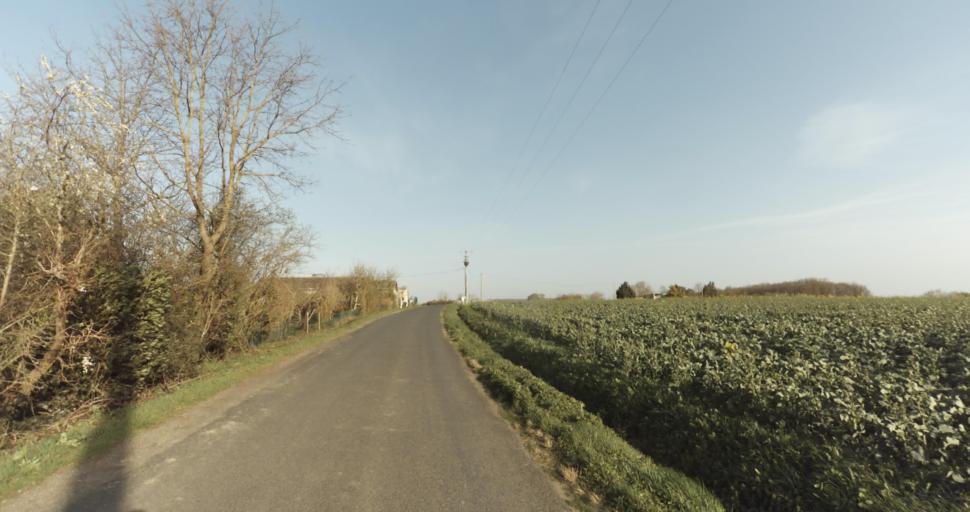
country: FR
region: Midi-Pyrenees
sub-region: Departement du Tarn
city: Saint-Sulpice-la-Pointe
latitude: 43.7337
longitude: 1.6943
